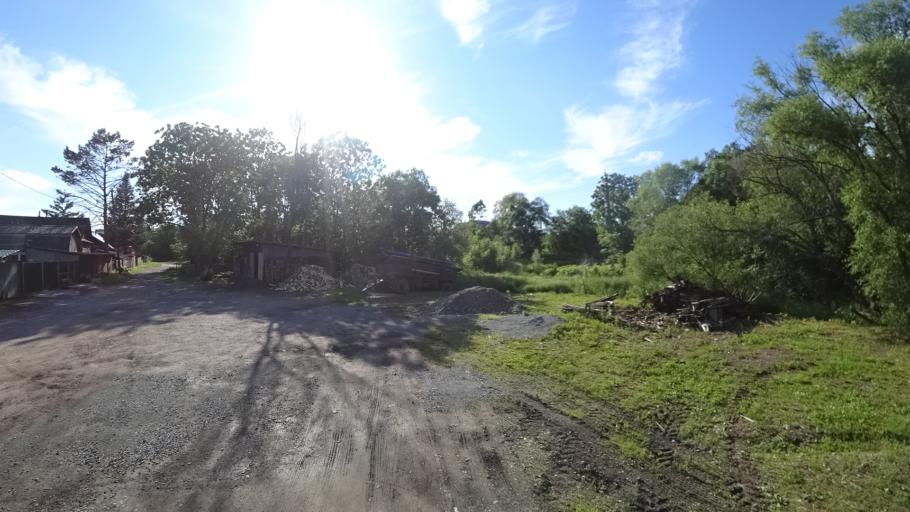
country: RU
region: Khabarovsk Krai
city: Khor
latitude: 47.8935
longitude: 134.9848
